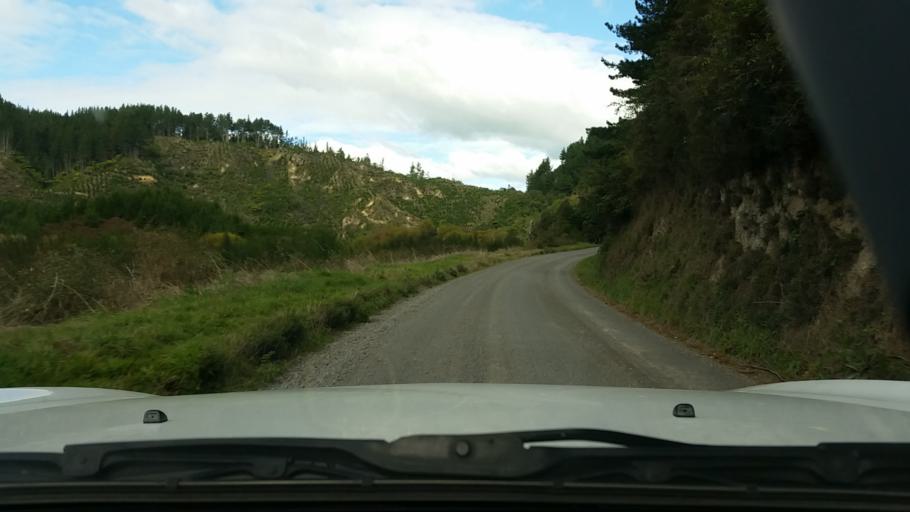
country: NZ
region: Waikato
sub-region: Taupo District
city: Taupo
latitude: -38.4641
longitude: 176.1612
